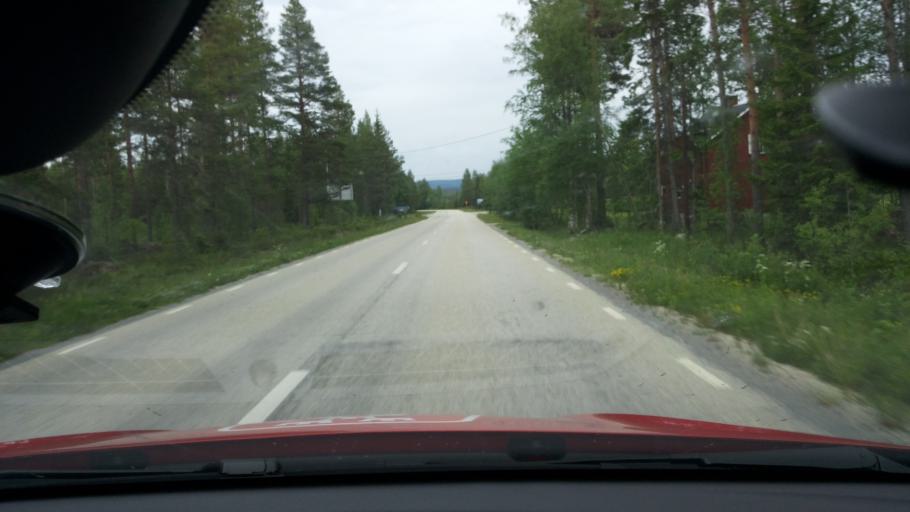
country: SE
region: Jaemtland
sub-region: Bergs Kommun
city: Hoverberg
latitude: 62.6413
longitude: 14.3519
